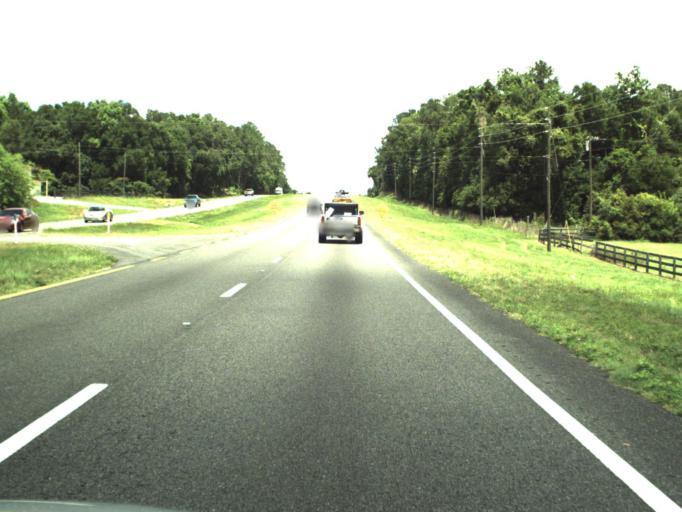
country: US
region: Florida
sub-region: Marion County
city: Citra
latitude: 29.3227
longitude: -82.1516
